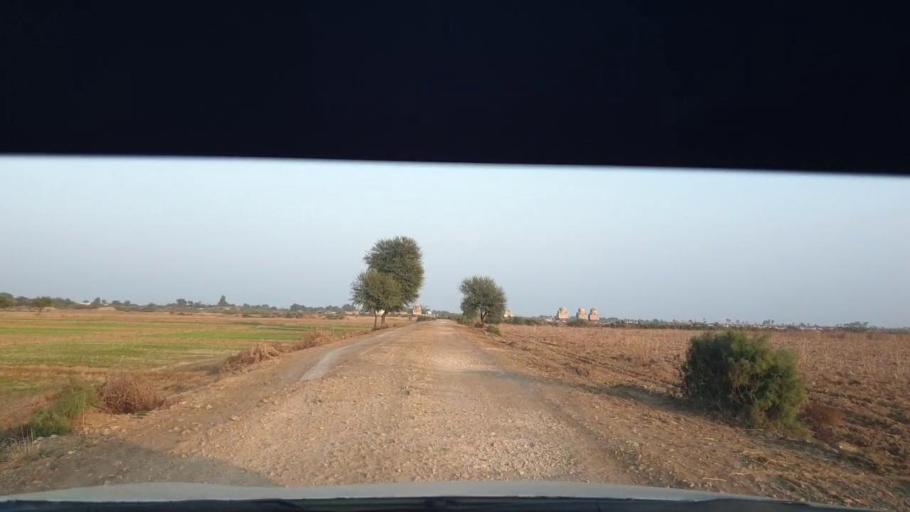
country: PK
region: Sindh
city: Berani
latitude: 25.7567
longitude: 68.9873
